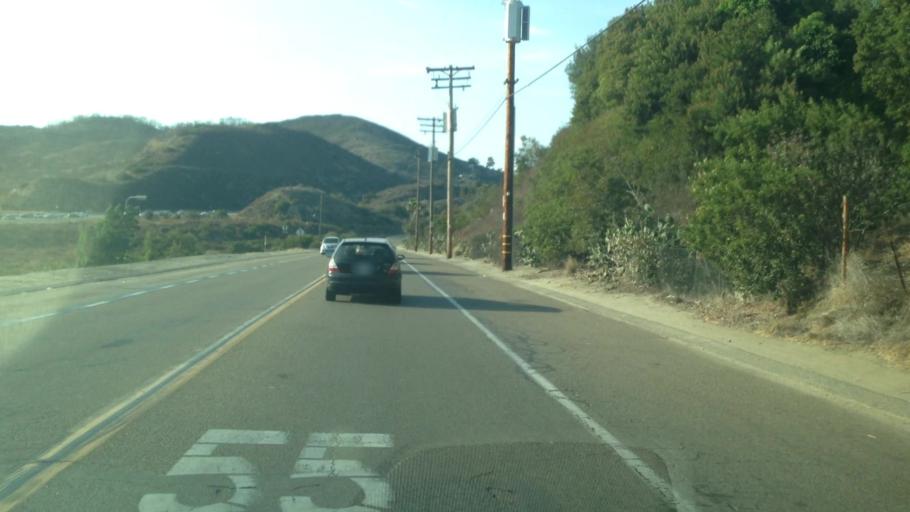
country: US
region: California
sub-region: San Diego County
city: Rainbow
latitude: 33.3874
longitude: -117.1724
